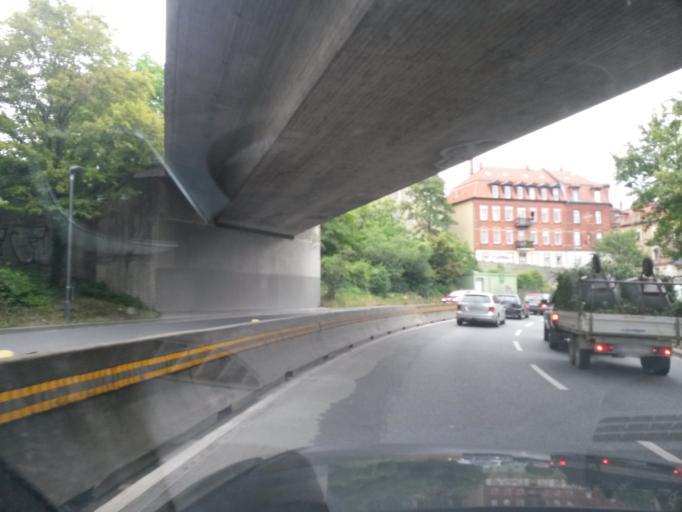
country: DE
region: Bavaria
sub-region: Regierungsbezirk Unterfranken
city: Wuerzburg
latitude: 49.8040
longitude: 9.9396
